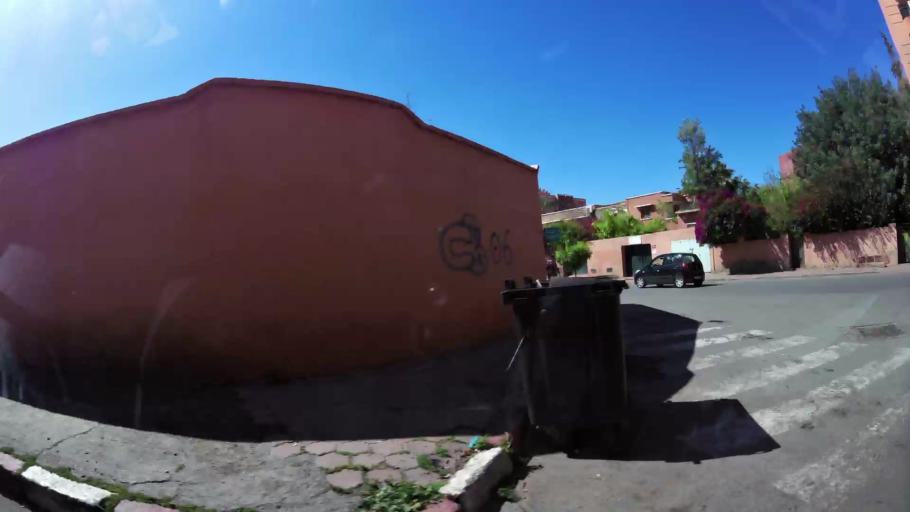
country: MA
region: Marrakech-Tensift-Al Haouz
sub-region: Marrakech
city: Marrakesh
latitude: 31.6380
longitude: -8.0056
